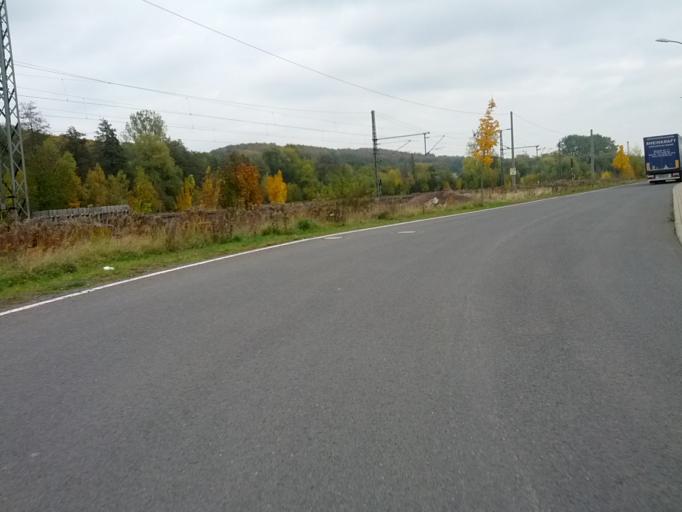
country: DE
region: Thuringia
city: Thal
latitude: 50.9547
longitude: 10.4024
